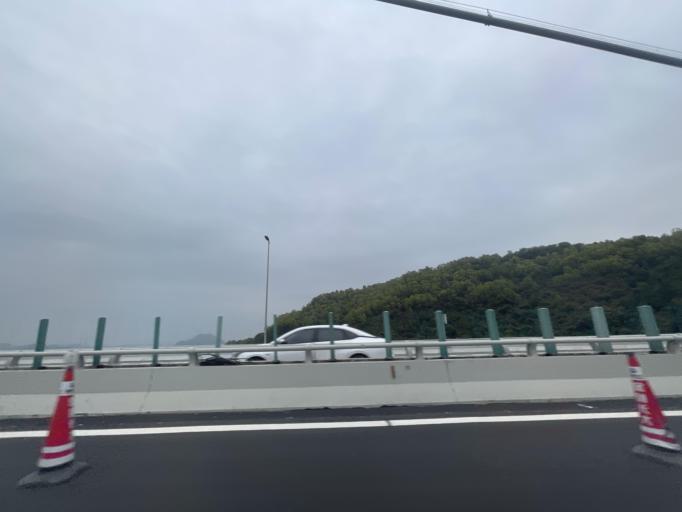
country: CN
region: Guangdong
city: Xinwan
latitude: 22.8000
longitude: 113.6206
